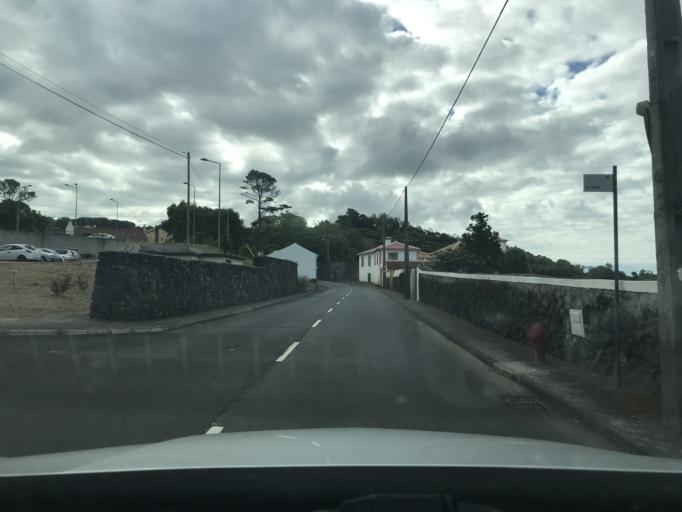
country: PT
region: Azores
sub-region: Angra do Heroismo
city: Angra do Heroismo
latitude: 38.6719
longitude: -27.2443
